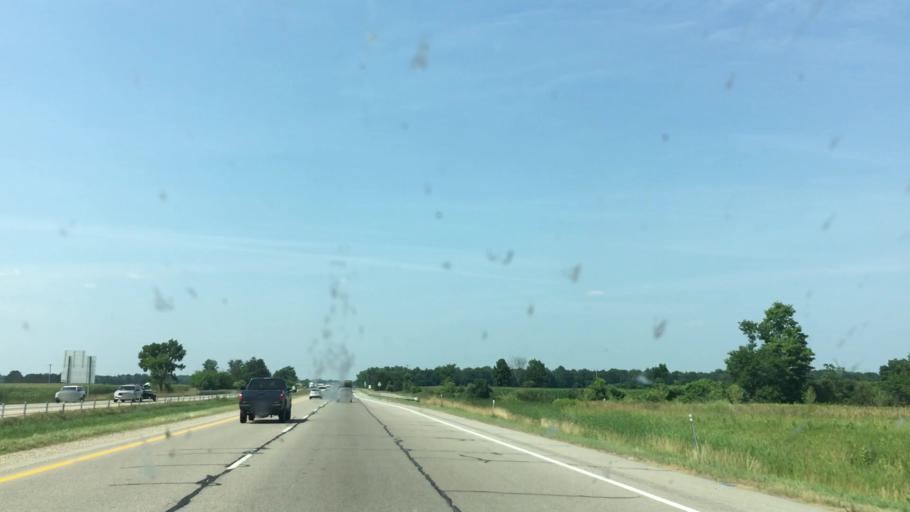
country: US
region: Michigan
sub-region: Allegan County
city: Wayland
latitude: 42.6343
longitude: -85.6621
